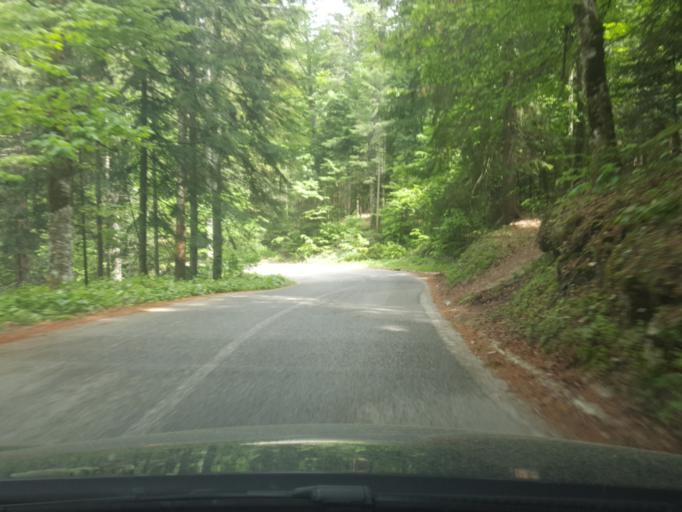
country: RS
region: Central Serbia
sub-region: Zlatiborski Okrug
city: Bajina Basta
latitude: 43.9180
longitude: 19.4879
